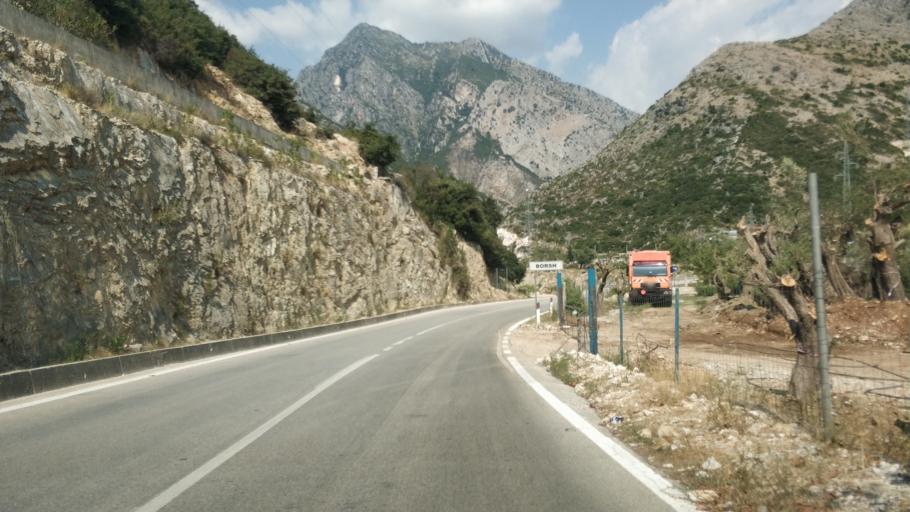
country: AL
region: Vlore
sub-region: Rrethi i Sarandes
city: Lukove
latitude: 40.0619
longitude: 19.8487
